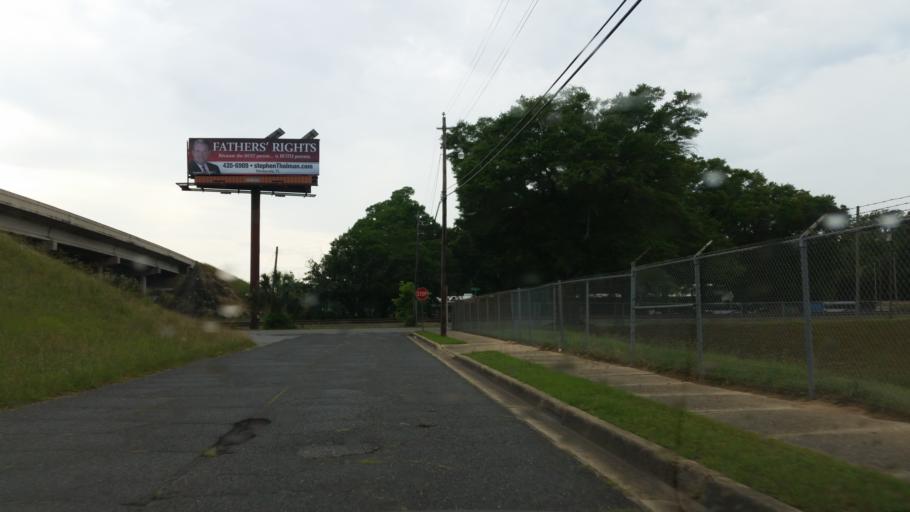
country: US
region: Florida
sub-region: Escambia County
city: Brent
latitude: 30.4695
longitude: -87.2359
